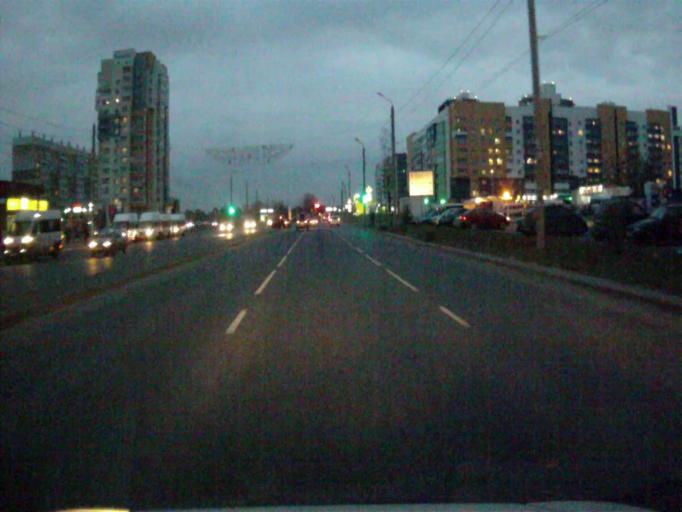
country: RU
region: Chelyabinsk
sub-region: Gorod Chelyabinsk
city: Chelyabinsk
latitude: 55.1642
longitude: 61.2949
